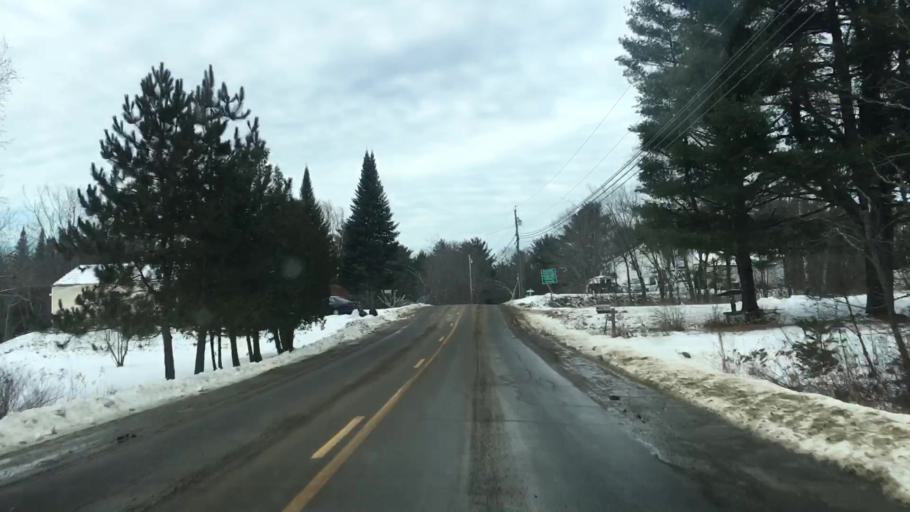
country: US
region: Maine
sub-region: Kennebec County
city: Chelsea
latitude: 44.2700
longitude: -69.6528
